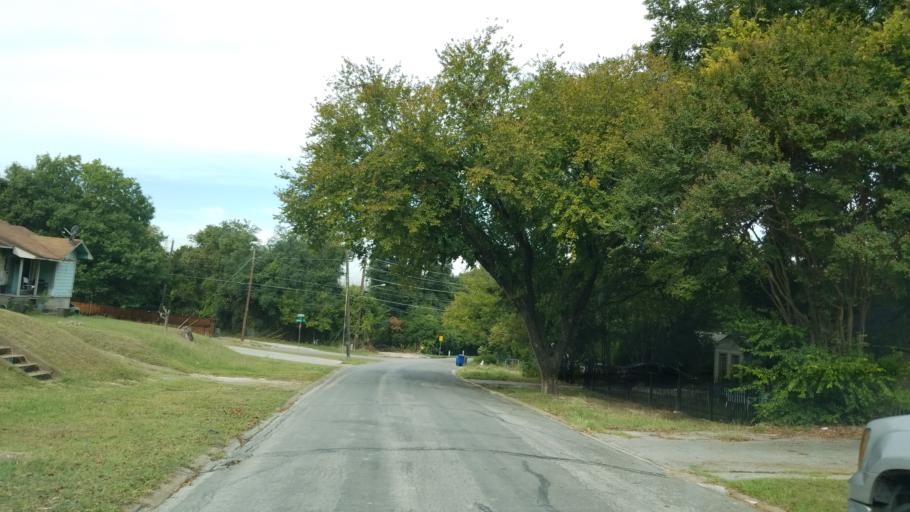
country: US
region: Texas
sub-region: Dallas County
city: Dallas
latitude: 32.7744
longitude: -96.7197
